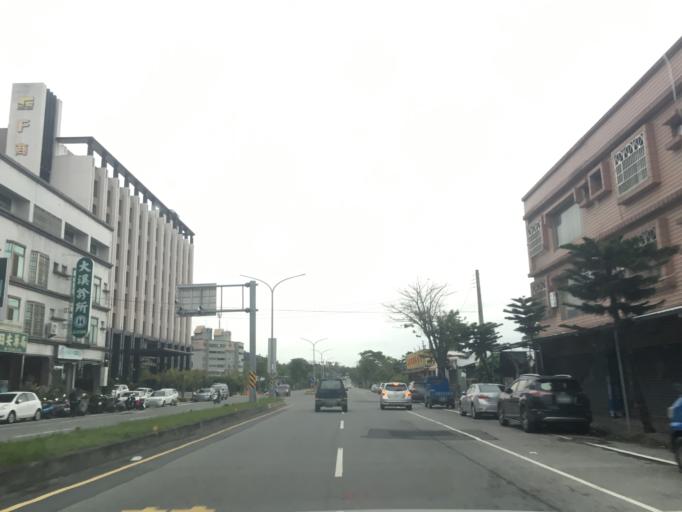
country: TW
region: Taiwan
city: Taitung City
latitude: 22.7068
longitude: 121.0421
